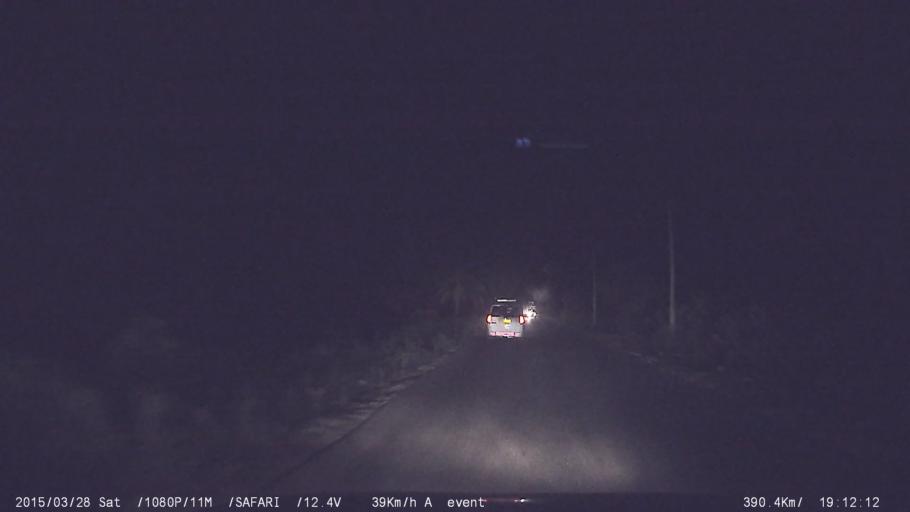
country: IN
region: Karnataka
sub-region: Mandya
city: Shrirangapattana
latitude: 12.3957
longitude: 76.6325
